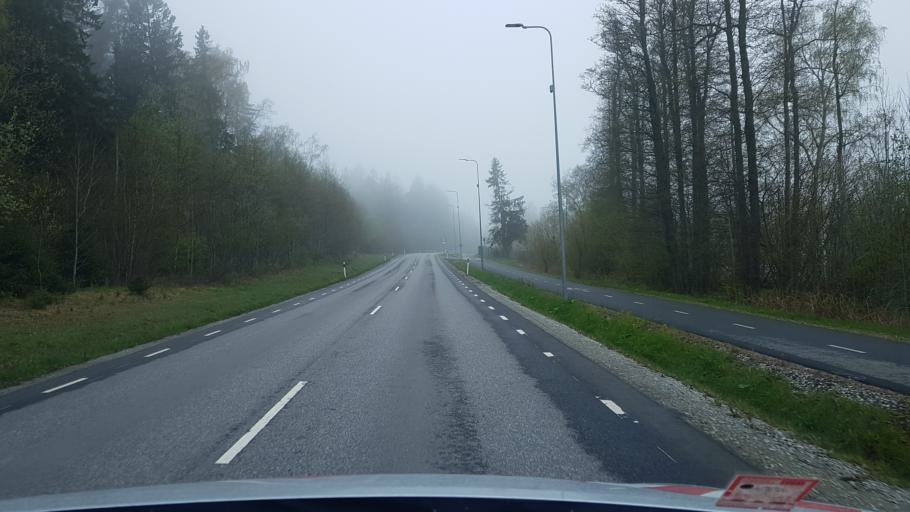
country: EE
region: Harju
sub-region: Viimsi vald
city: Viimsi
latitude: 59.5269
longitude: 24.8811
